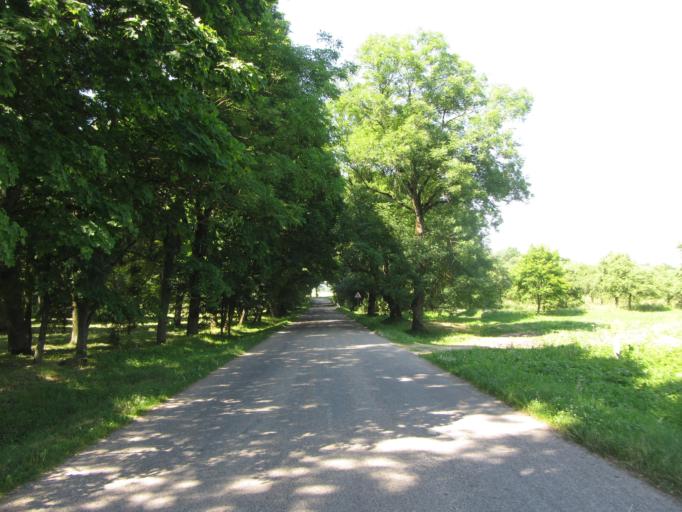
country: LT
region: Vilnius County
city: Ukmerge
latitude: 55.2710
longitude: 24.9380
